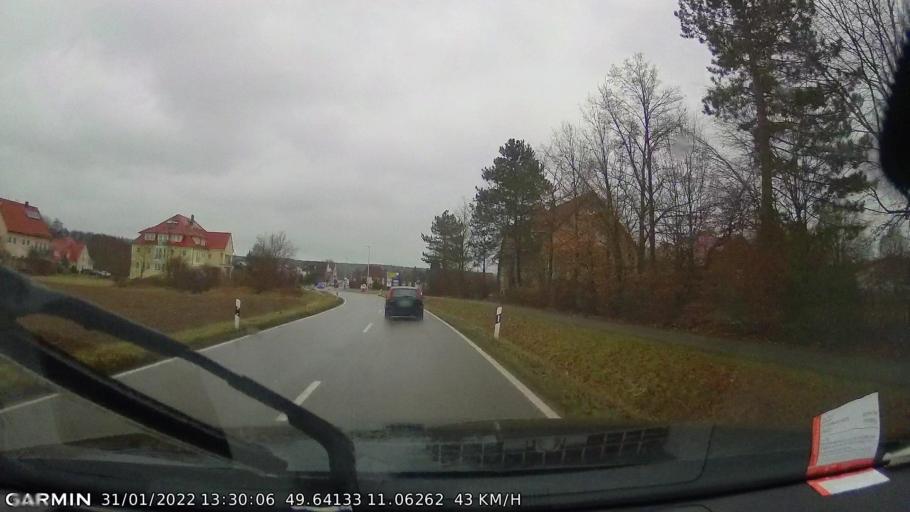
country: DE
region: Bavaria
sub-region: Upper Franconia
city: Langensendelbach
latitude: 49.6413
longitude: 11.0629
